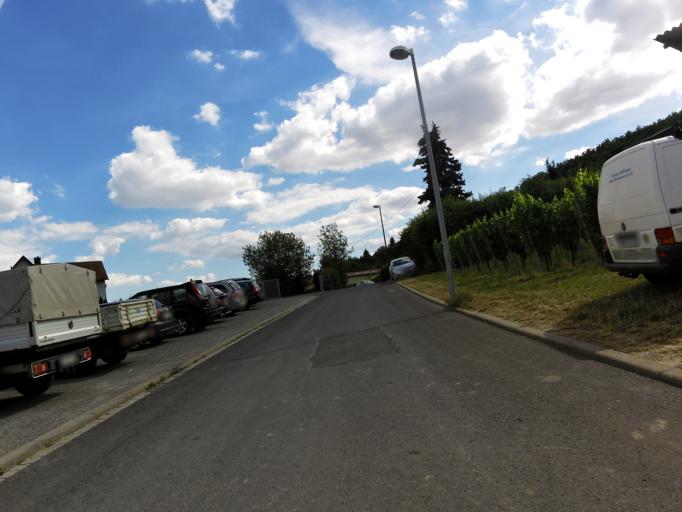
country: DE
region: Bavaria
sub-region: Regierungsbezirk Unterfranken
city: Randersacker
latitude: 49.7544
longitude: 9.9676
